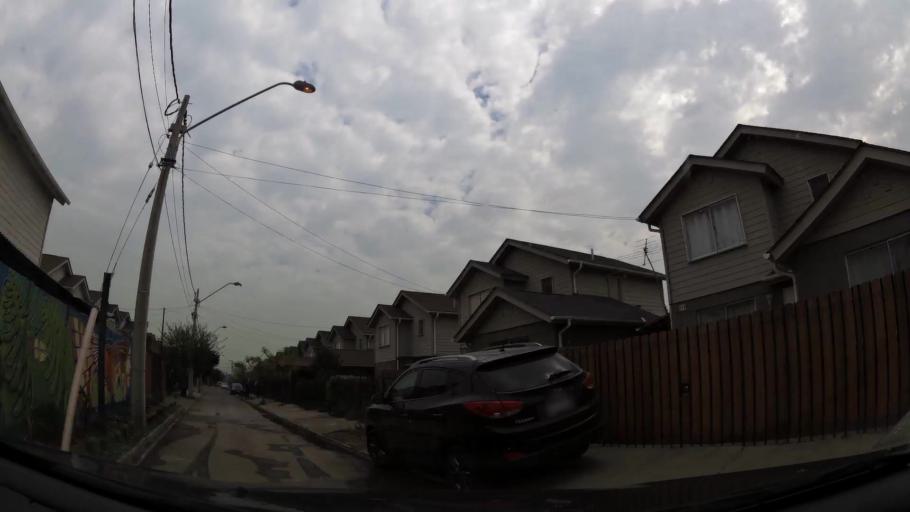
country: CL
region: Santiago Metropolitan
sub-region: Provincia de Chacabuco
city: Chicureo Abajo
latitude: -33.2108
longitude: -70.6865
